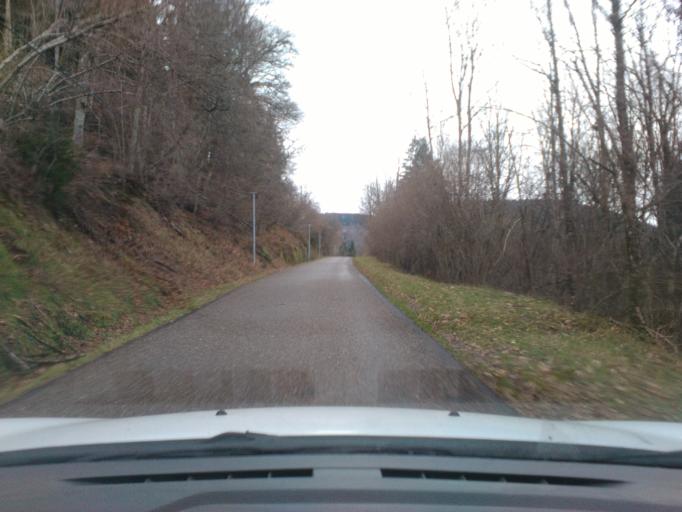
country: FR
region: Lorraine
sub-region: Departement des Vosges
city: La Bresse
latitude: 47.9755
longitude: 6.8653
